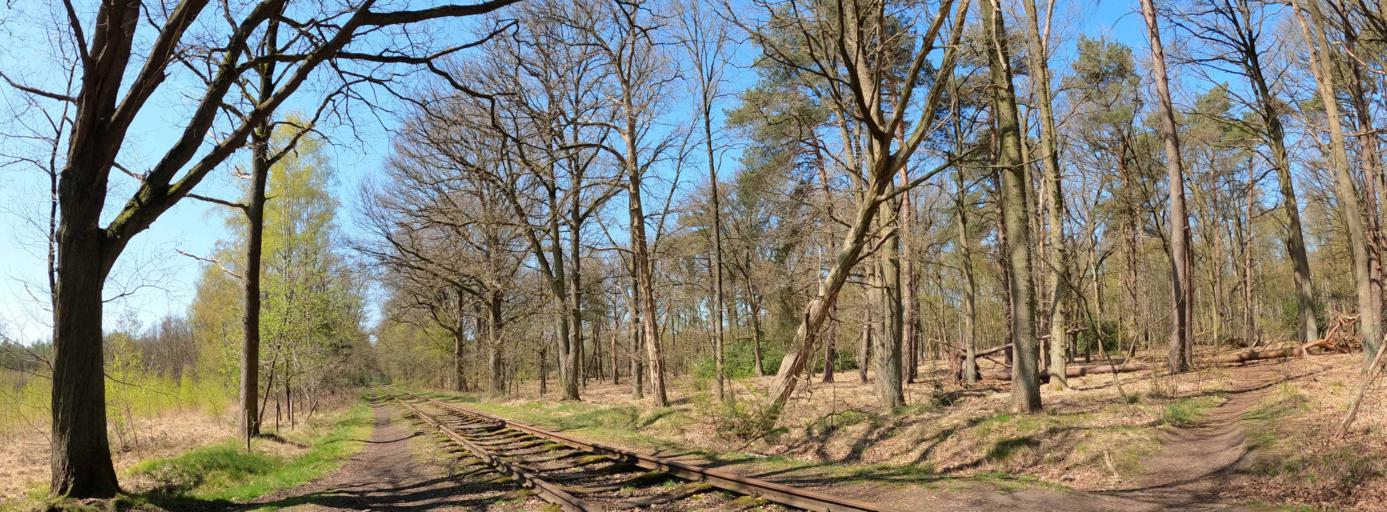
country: BE
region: Flanders
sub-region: Provincie Antwerpen
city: Brasschaat
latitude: 51.3348
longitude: 4.4880
